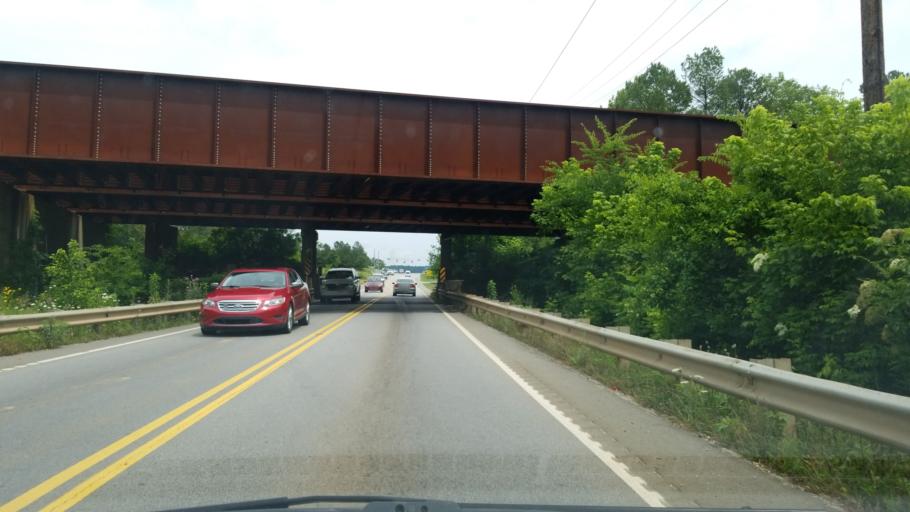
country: US
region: Tennessee
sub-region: Hamilton County
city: Harrison
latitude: 35.0726
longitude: -85.1601
